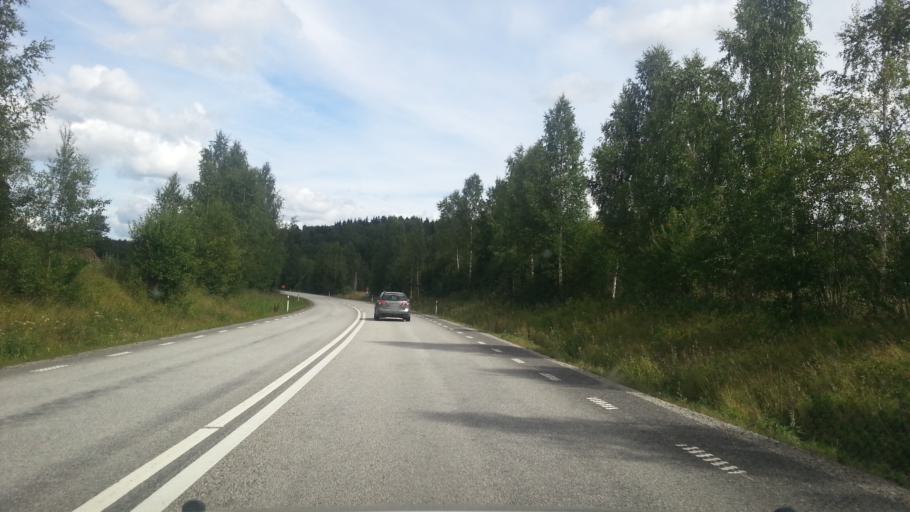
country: SE
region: OErebro
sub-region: Lindesbergs Kommun
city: Lindesberg
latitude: 59.6389
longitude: 15.2254
